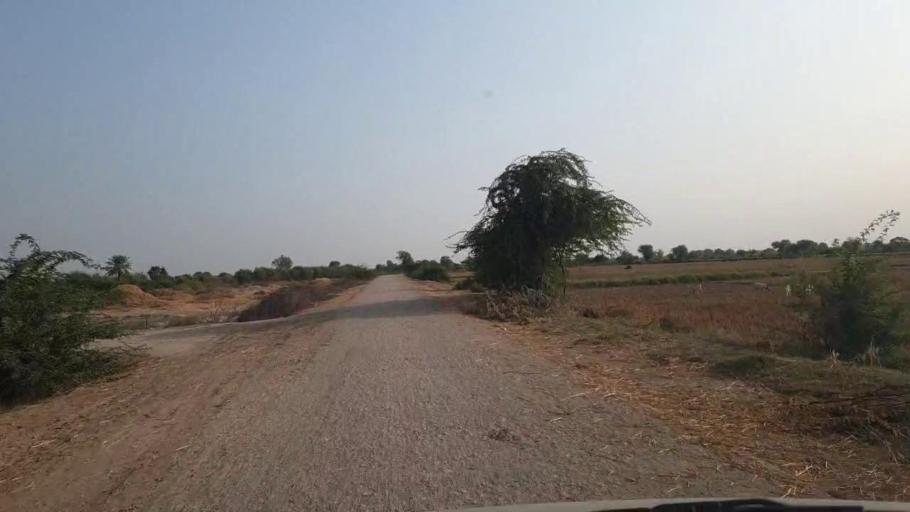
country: PK
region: Sindh
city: Rajo Khanani
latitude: 25.0158
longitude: 68.7862
